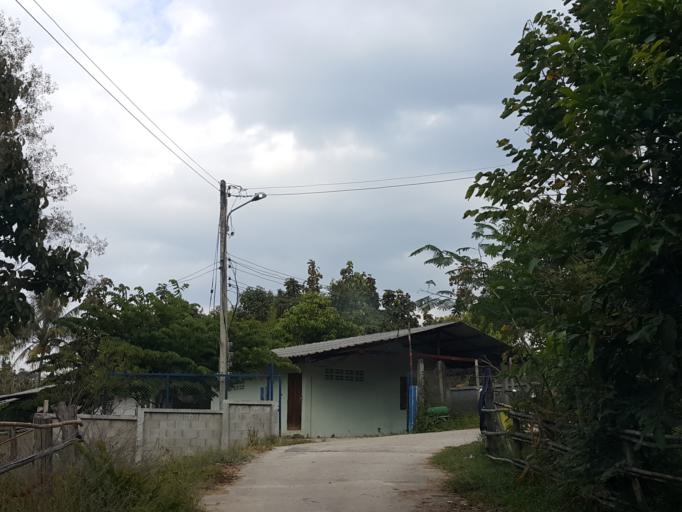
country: TH
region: Chiang Mai
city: Om Koi
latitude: 17.7990
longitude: 98.3370
